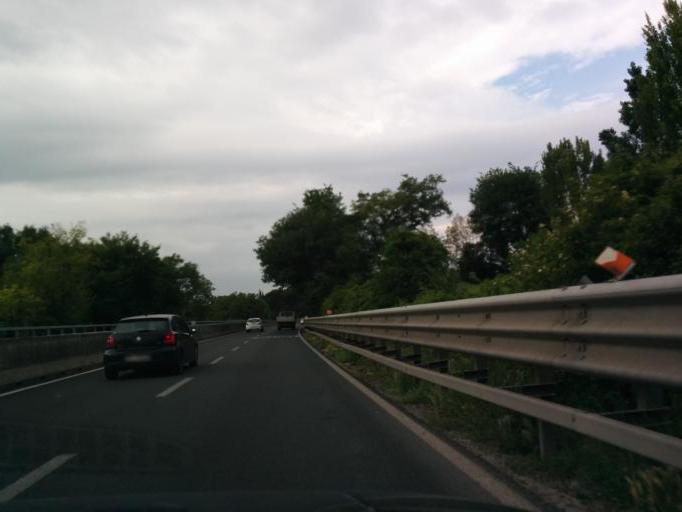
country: IT
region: Tuscany
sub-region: Province of Florence
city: San Casciano in Val di Pesa
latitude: 43.6238
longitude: 11.1842
